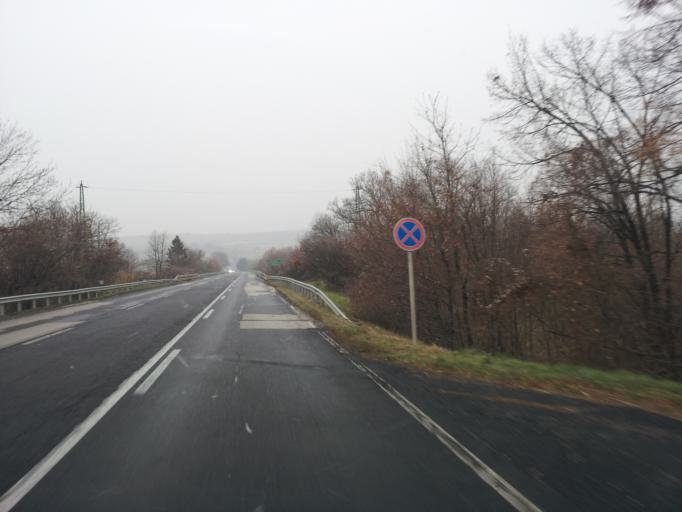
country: HU
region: Veszprem
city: Urkut
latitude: 47.1486
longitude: 17.6685
